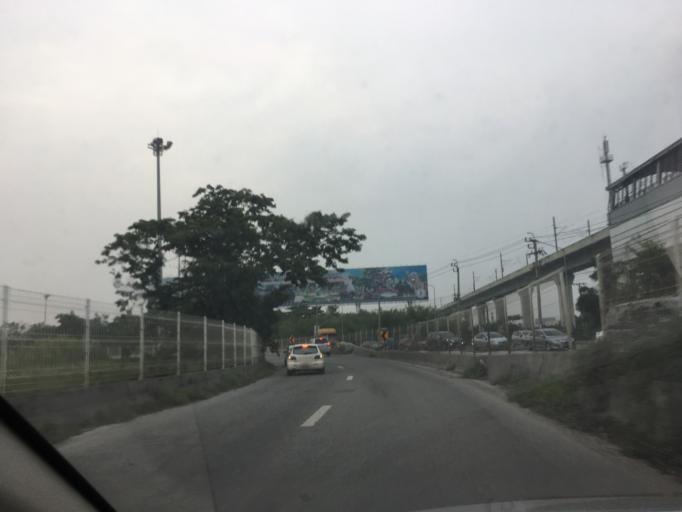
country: TH
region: Bangkok
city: Lat Krabang
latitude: 13.7282
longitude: 100.7486
